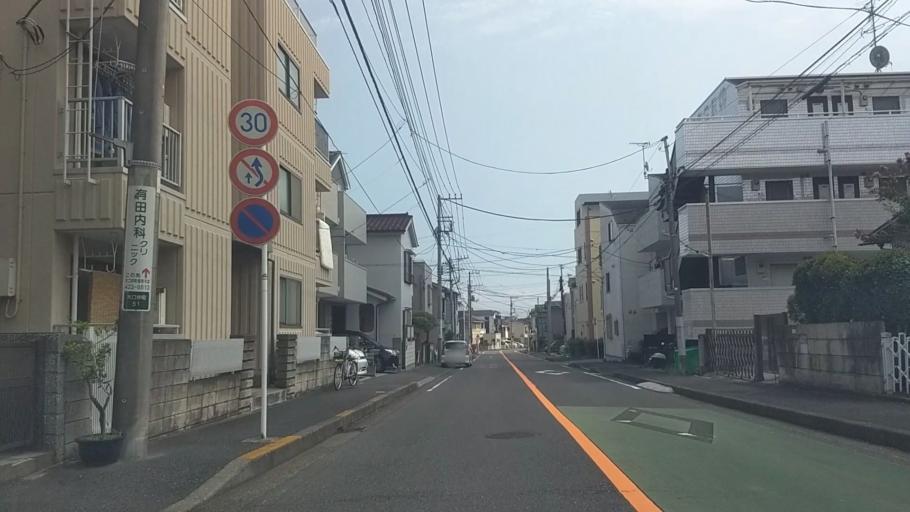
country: JP
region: Kanagawa
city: Yokohama
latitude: 35.4933
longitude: 139.6398
